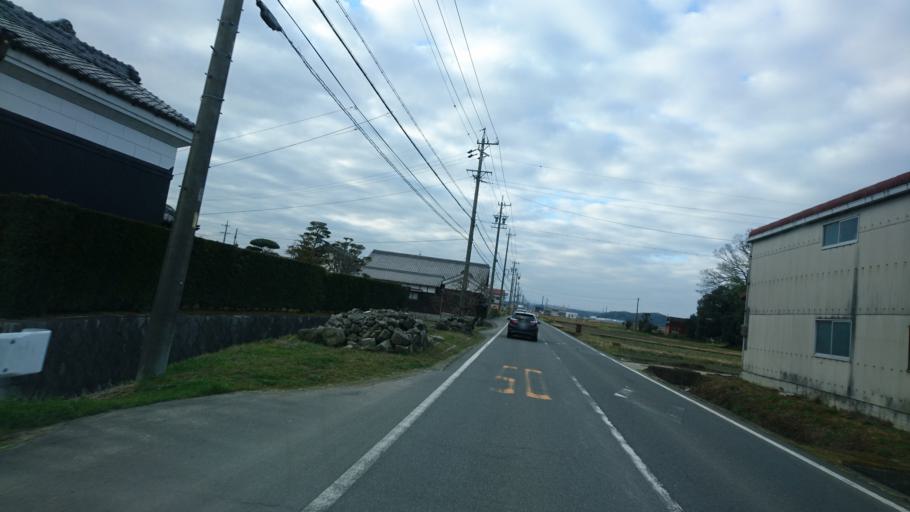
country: JP
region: Mie
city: Ueno-ebisumachi
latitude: 34.7572
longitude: 136.1115
